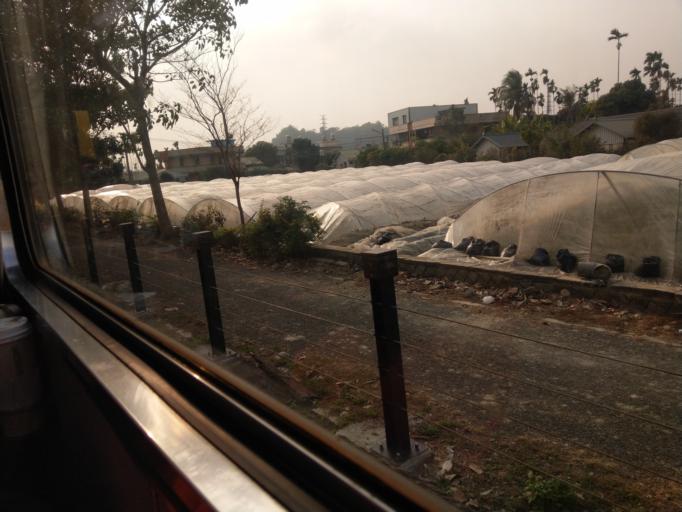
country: TW
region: Taiwan
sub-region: Chiayi
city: Jiayi Shi
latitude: 23.5052
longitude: 120.5325
